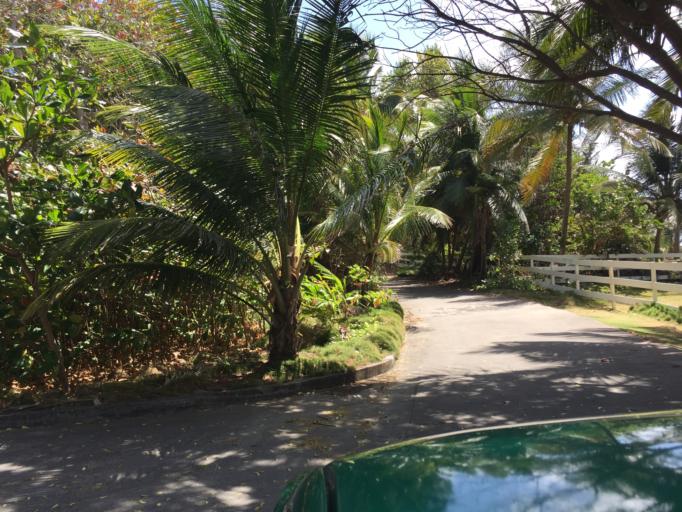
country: VC
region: Grenadines
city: Port Elizabeth
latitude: 13.0255
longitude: -61.2174
